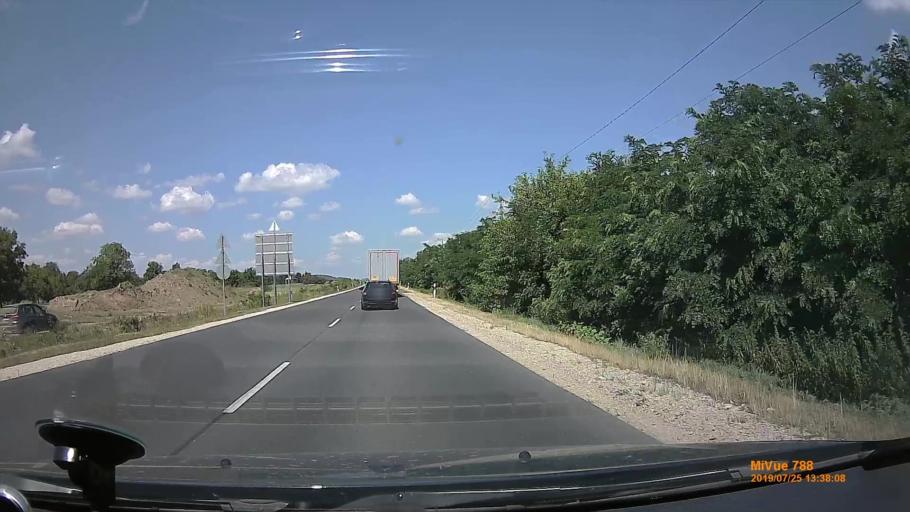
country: HU
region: Borsod-Abauj-Zemplen
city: Encs
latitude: 48.4127
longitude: 21.1765
